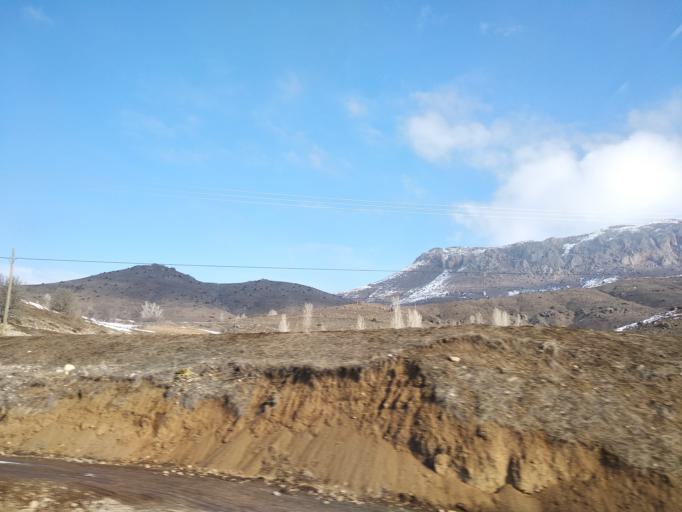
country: TR
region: Gumushane
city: Kelkit
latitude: 40.0130
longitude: 39.5322
